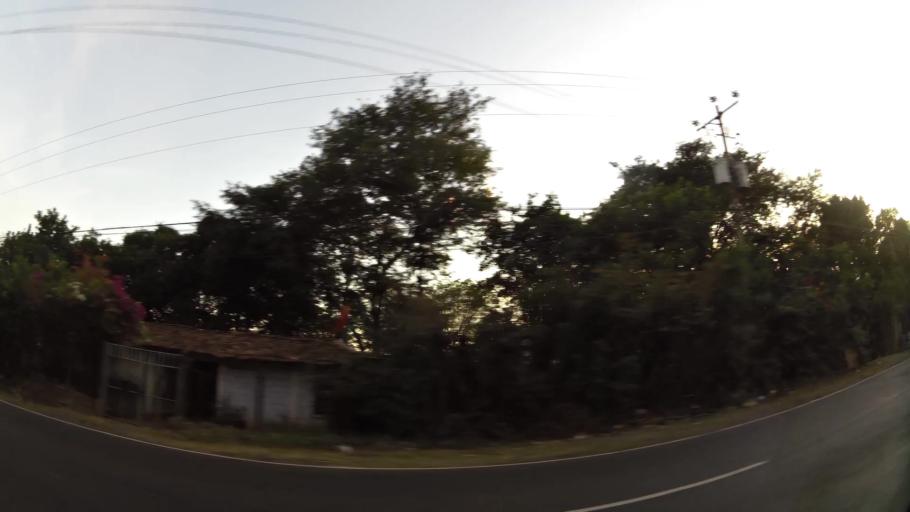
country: SV
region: San Miguel
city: San Miguel
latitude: 13.4992
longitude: -88.2102
